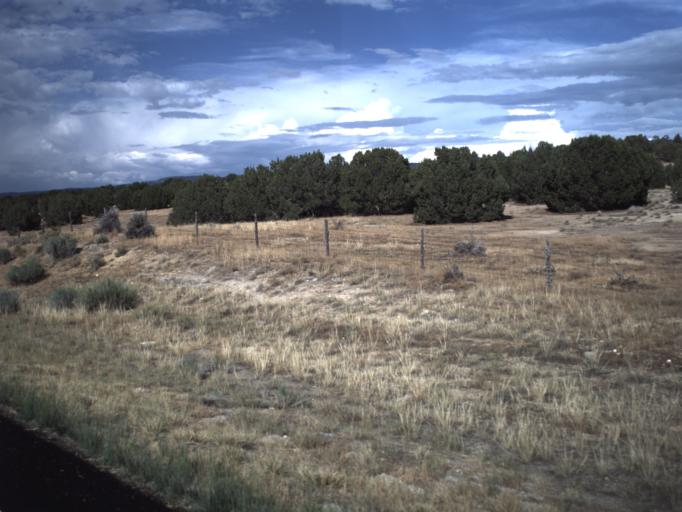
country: US
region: Utah
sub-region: Sanpete County
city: Moroni
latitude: 39.4665
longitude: -111.5332
